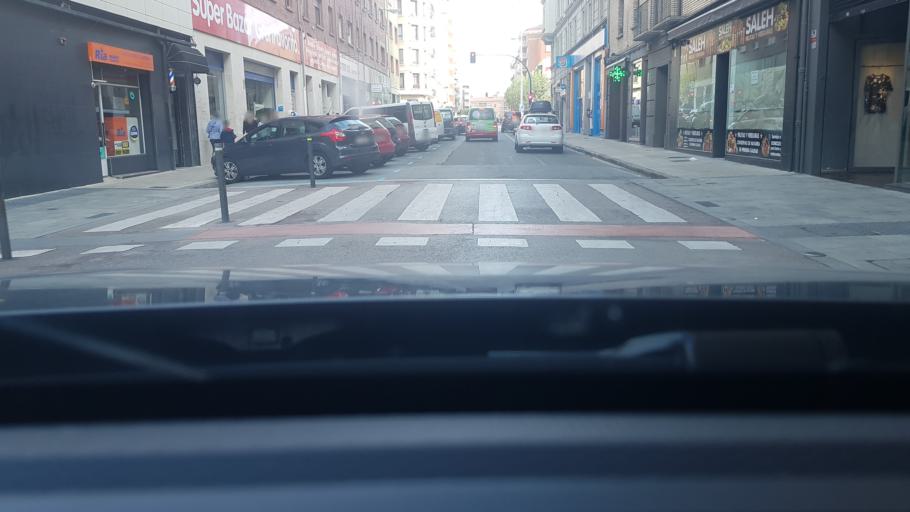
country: ES
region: Navarre
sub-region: Provincia de Navarra
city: Segundo Ensanche
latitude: 42.8103
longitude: -1.6388
